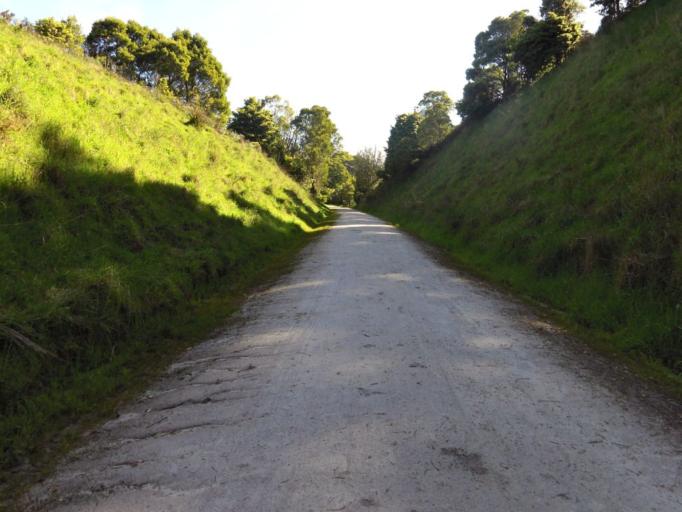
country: AU
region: Victoria
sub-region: Latrobe
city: Morwell
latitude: -38.6839
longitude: 146.1528
